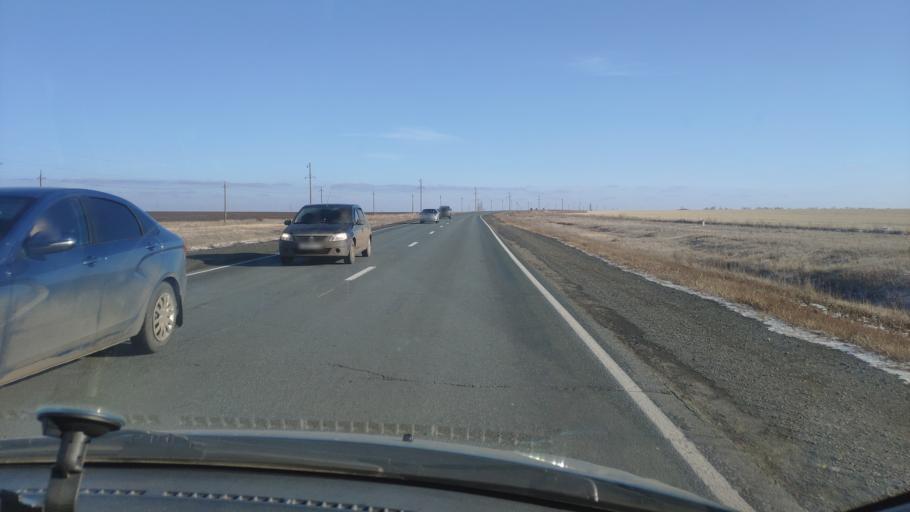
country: RU
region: Orenburg
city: Mednogorsk
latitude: 51.4354
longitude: 57.8942
